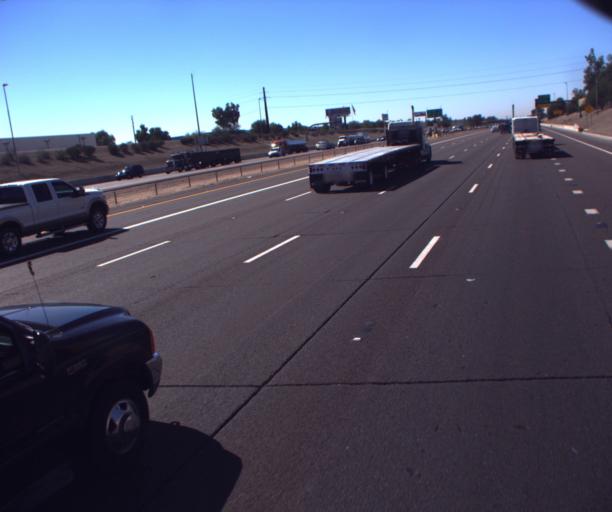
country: US
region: Arizona
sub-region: Maricopa County
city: Tolleson
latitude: 33.4629
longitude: -112.2096
